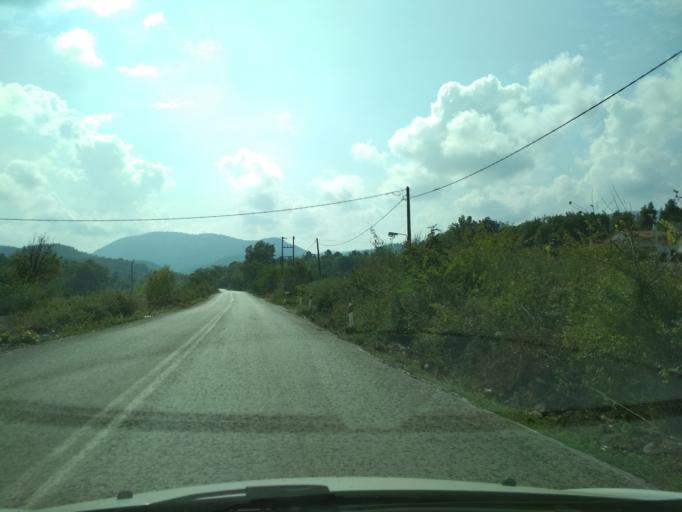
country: GR
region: Central Greece
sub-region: Nomos Evvoias
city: Prokopion
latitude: 38.7326
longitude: 23.4969
